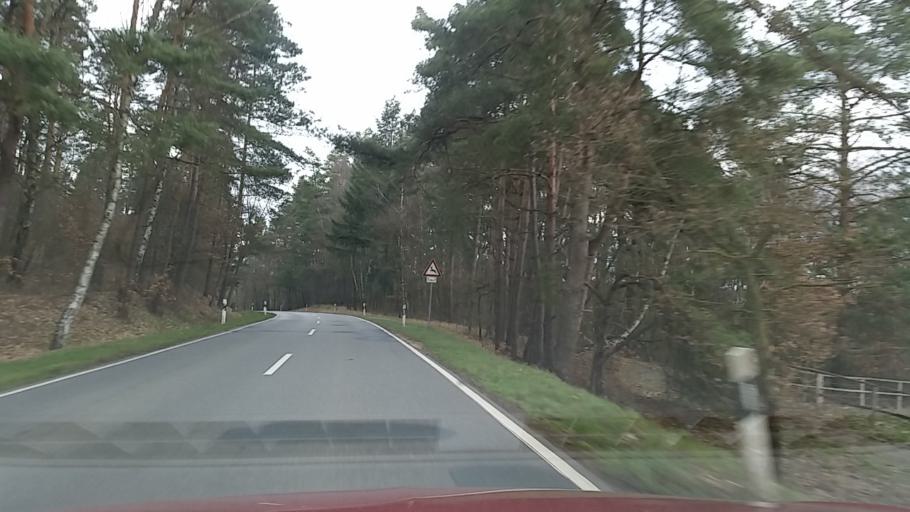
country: DE
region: Lower Saxony
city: Zernien
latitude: 53.0991
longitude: 10.9459
